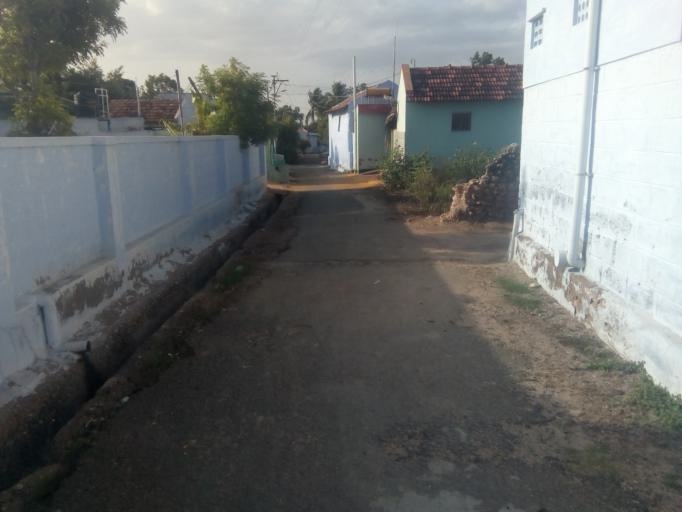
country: IN
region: Tamil Nadu
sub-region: Coimbatore
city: Annur
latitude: 11.1466
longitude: 77.1242
